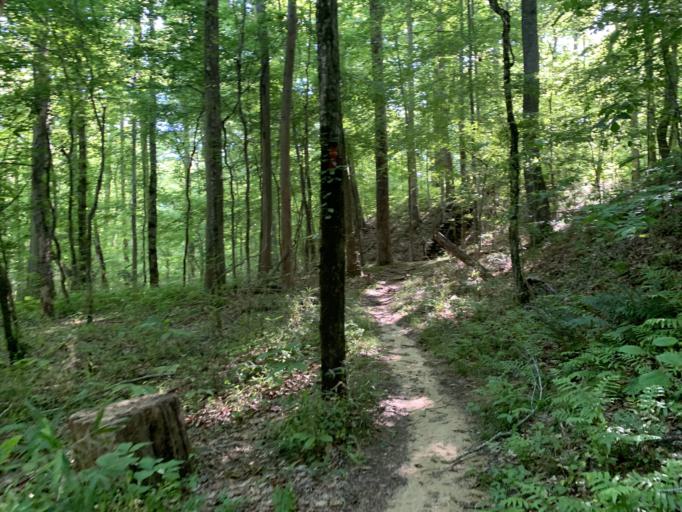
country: US
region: Tennessee
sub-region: Chester County
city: Henderson
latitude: 35.4914
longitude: -88.6785
